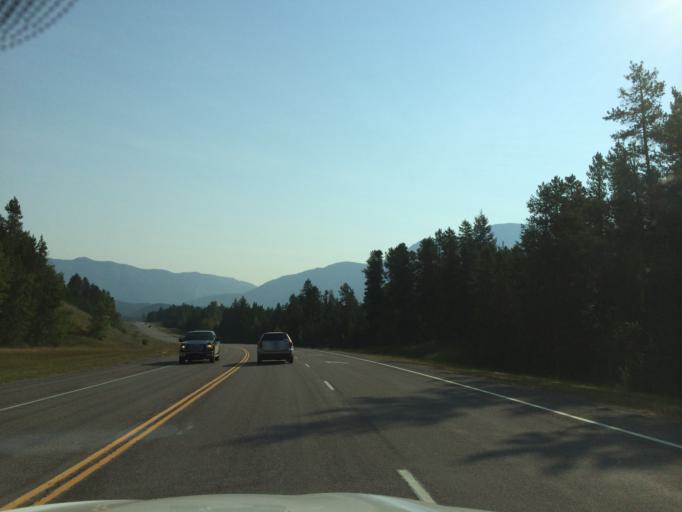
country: US
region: Montana
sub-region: Flathead County
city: Columbia Falls
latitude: 48.4521
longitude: -114.0179
